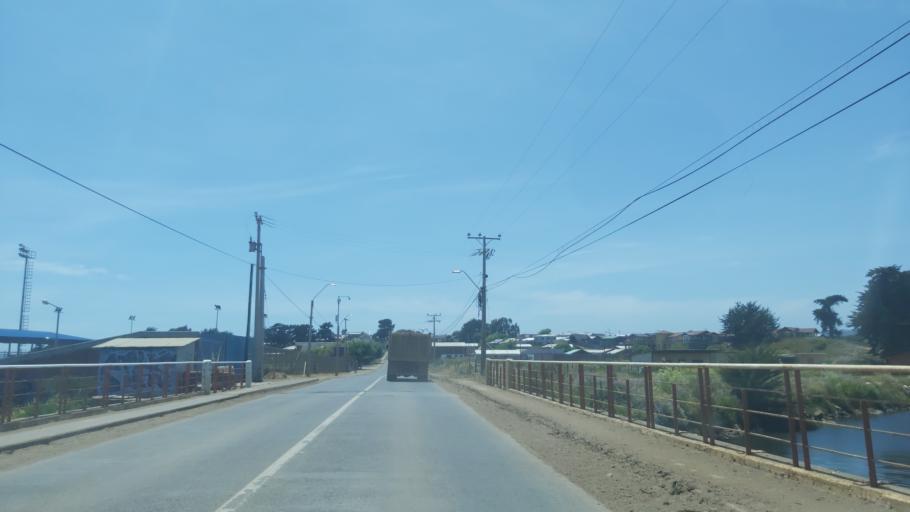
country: CL
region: Maule
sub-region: Provincia de Cauquenes
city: Cauquenes
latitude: -35.8079
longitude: -72.5697
